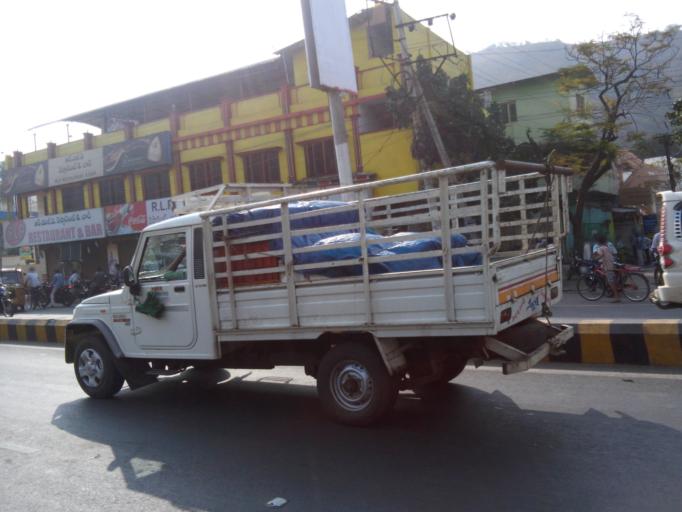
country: IN
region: Andhra Pradesh
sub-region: Krishna
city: Vijayawada
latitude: 16.5172
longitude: 80.6446
